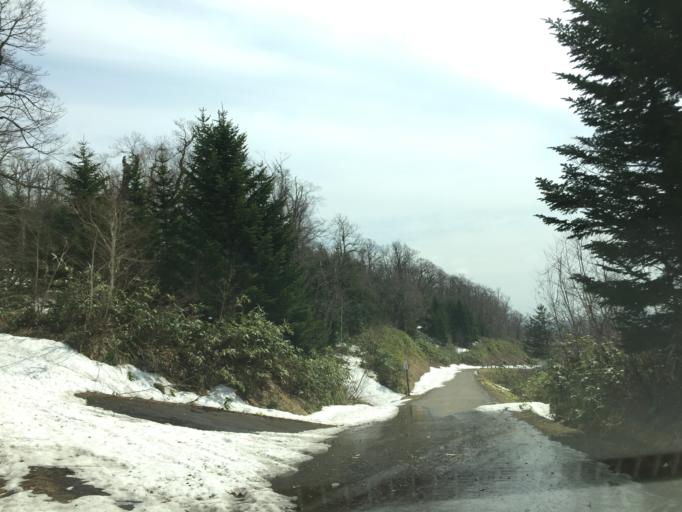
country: JP
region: Hokkaido
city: Akabira
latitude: 43.6076
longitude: 142.0684
